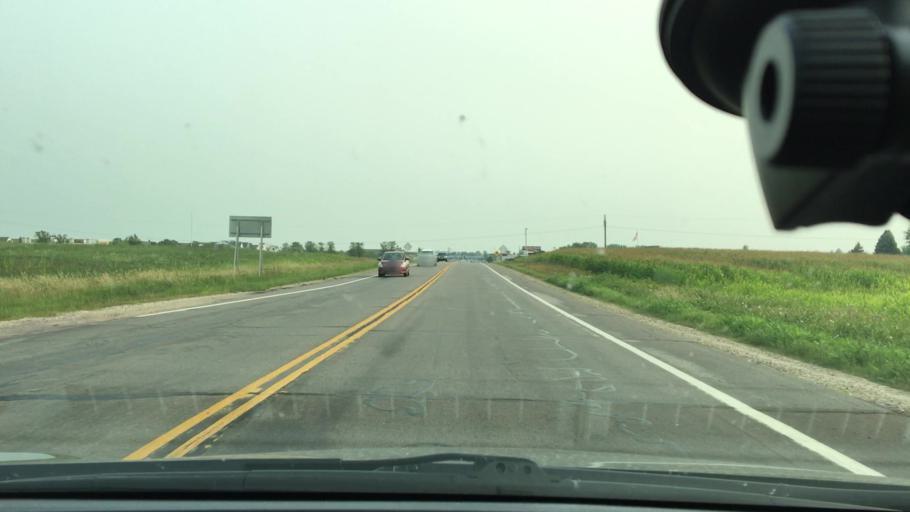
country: US
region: Minnesota
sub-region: Wright County
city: Albertville
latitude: 45.2515
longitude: -93.6633
